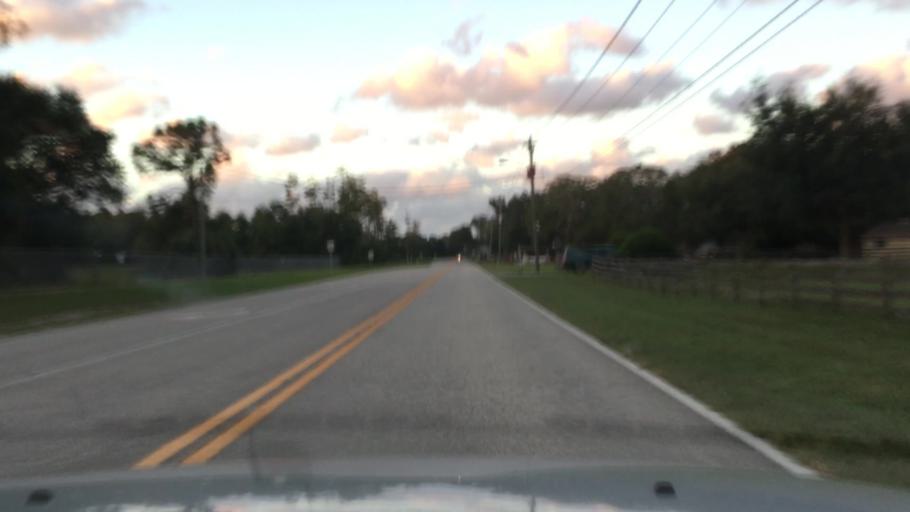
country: US
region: Florida
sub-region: Volusia County
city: Ormond Beach
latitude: 29.2766
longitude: -81.1129
